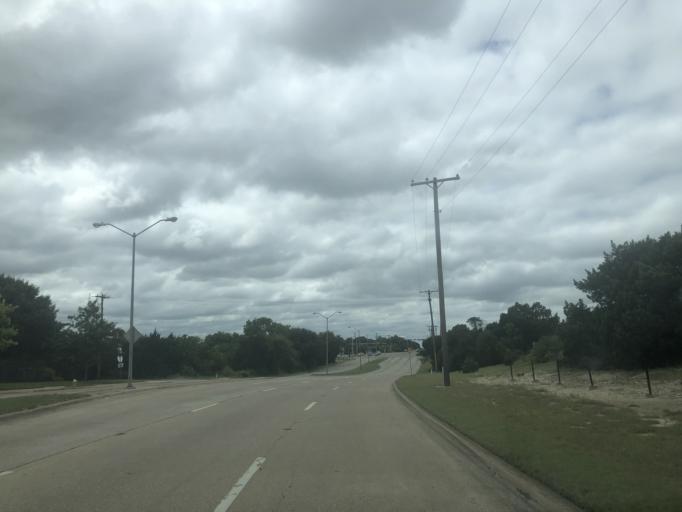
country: US
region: Texas
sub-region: Dallas County
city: Duncanville
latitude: 32.6648
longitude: -96.9434
